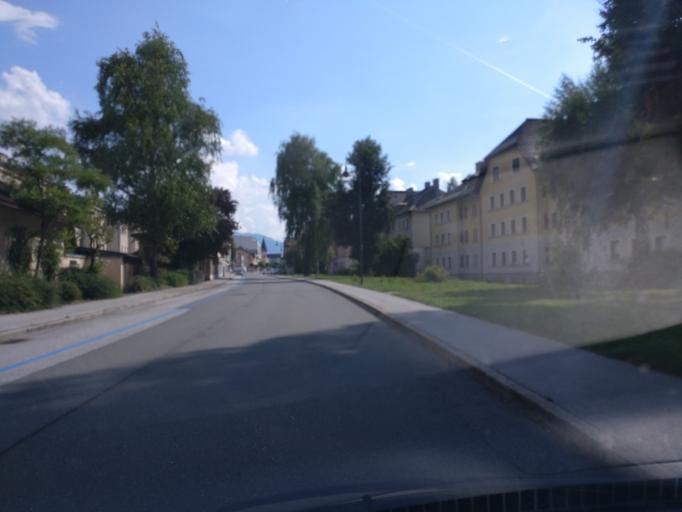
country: AT
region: Salzburg
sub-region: Politischer Bezirk Sankt Johann im Pongau
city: Bischofshofen
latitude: 47.4200
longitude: 13.2188
